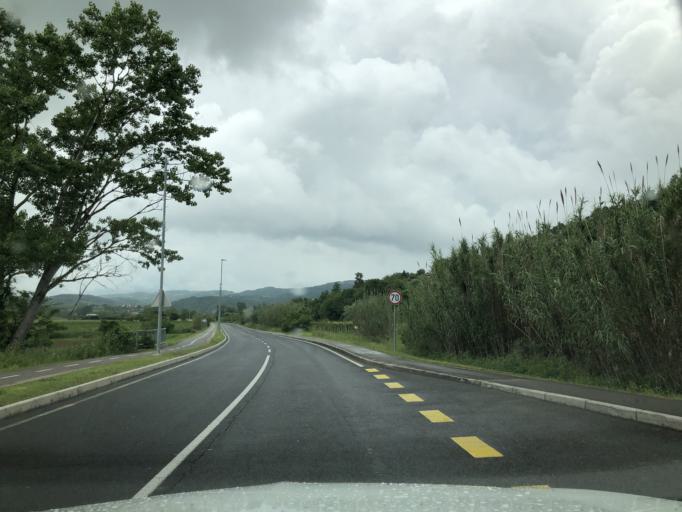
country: SI
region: Koper-Capodistria
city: Koper
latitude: 45.5194
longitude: 13.7484
